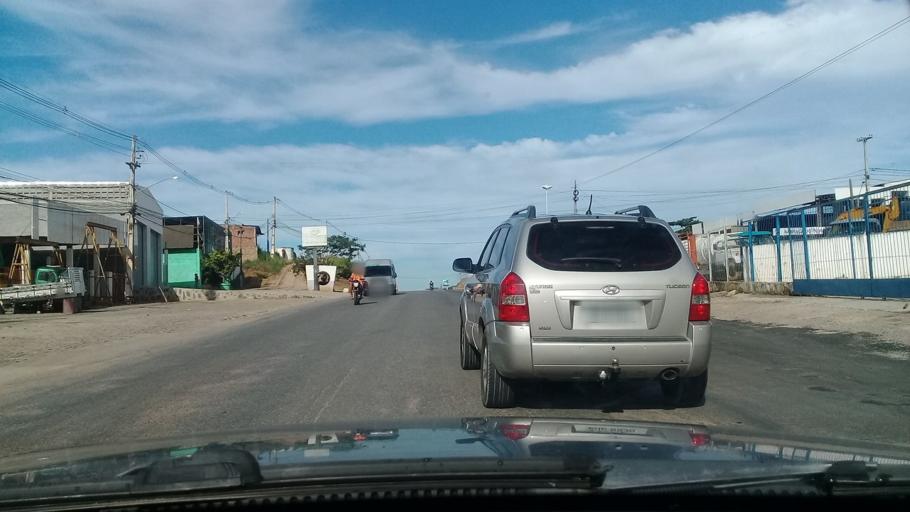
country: BR
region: Pernambuco
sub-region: Vitoria De Santo Antao
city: Vitoria de Santo Antao
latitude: -8.1146
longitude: -35.2792
